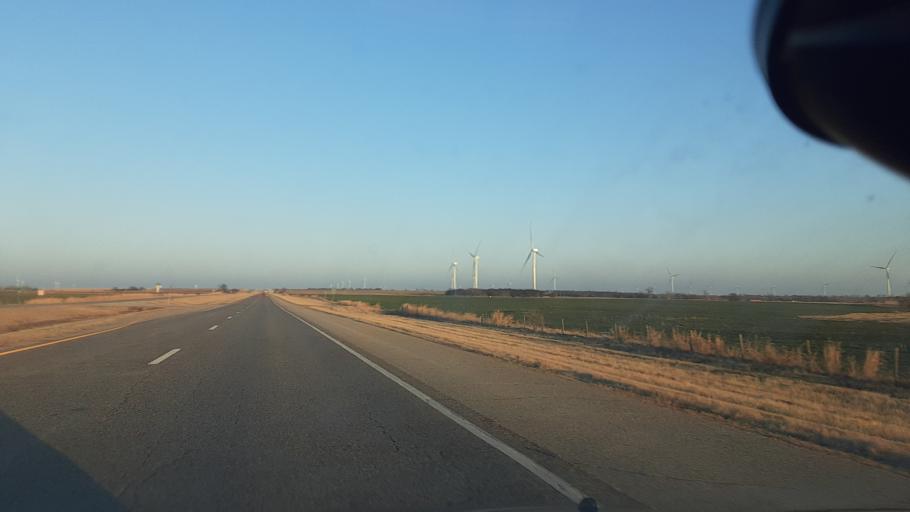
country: US
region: Oklahoma
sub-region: Noble County
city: Perry
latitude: 36.3983
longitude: -97.4714
